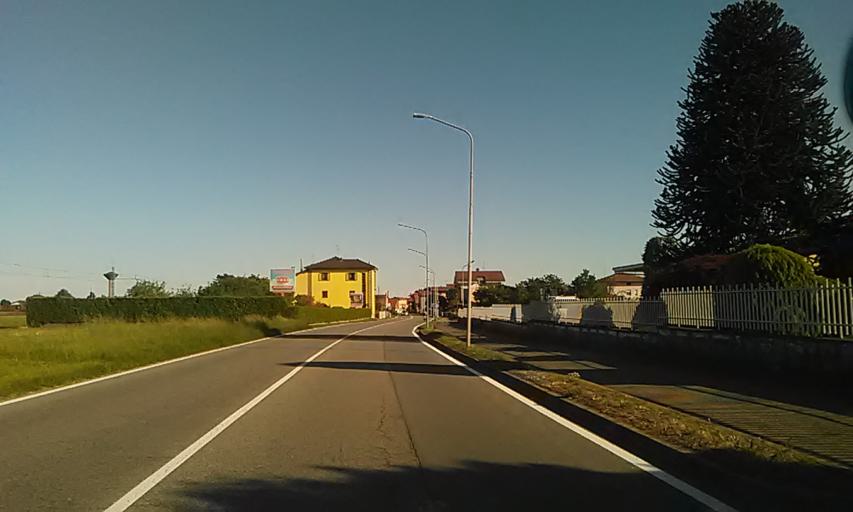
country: IT
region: Piedmont
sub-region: Provincia di Novara
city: Momo
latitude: 45.5814
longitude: 8.5508
